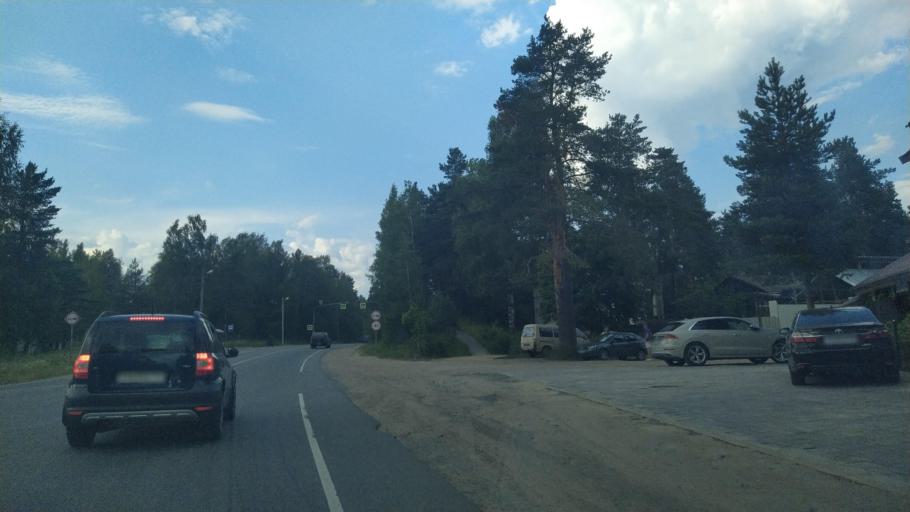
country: RU
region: Leningrad
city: Toksovo
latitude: 60.1516
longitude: 30.5220
